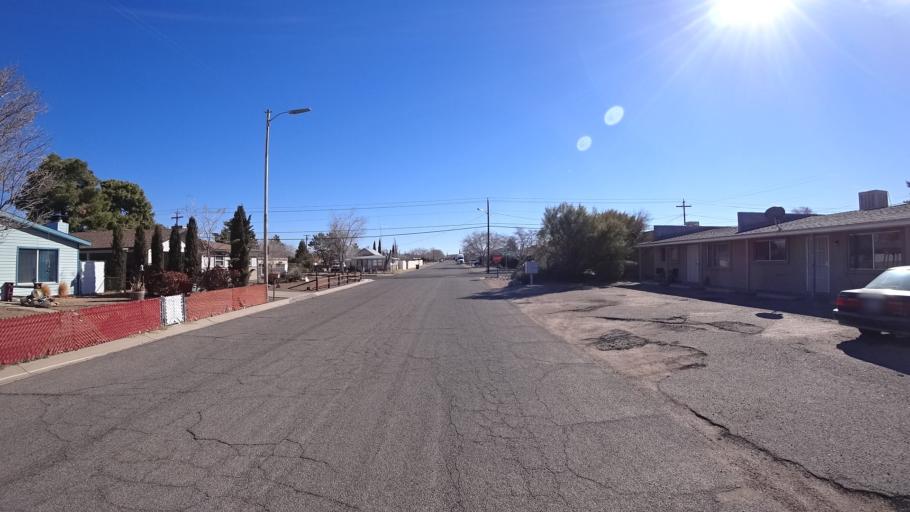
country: US
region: Arizona
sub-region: Mohave County
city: Kingman
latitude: 35.2075
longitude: -114.0296
